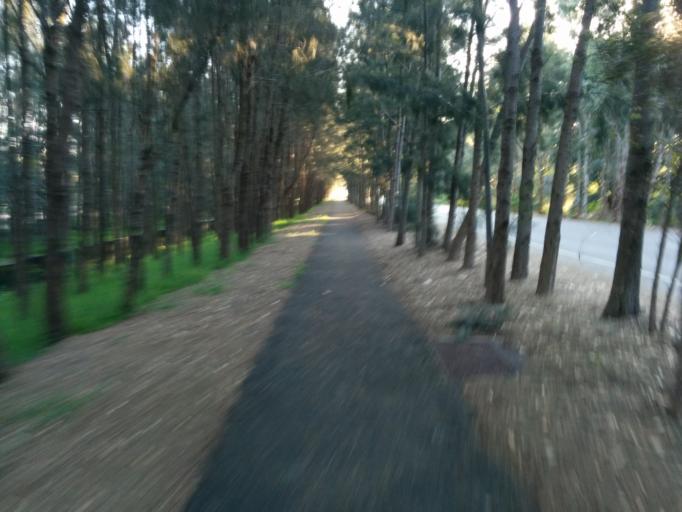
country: AU
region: New South Wales
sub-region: Canada Bay
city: Concord West
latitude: -33.8389
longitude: 151.0713
